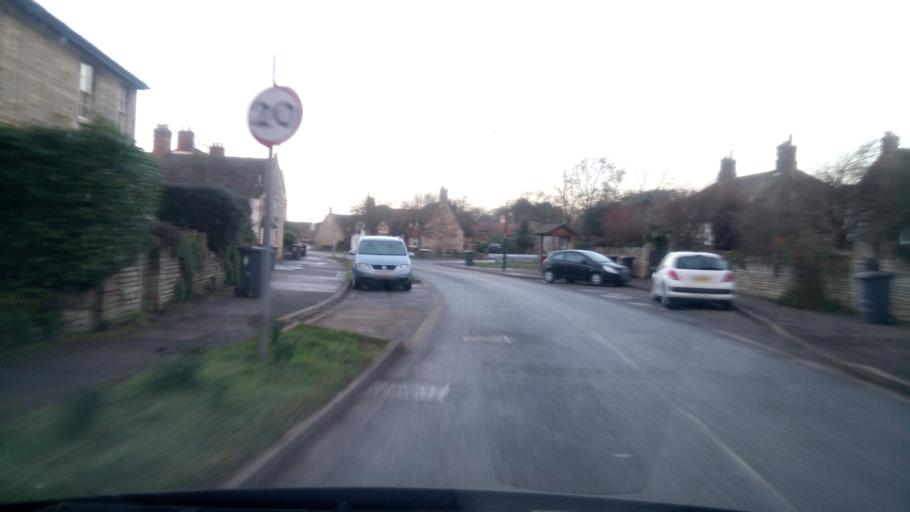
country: GB
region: England
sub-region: Peterborough
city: Castor
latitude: 52.5713
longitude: -0.3415
